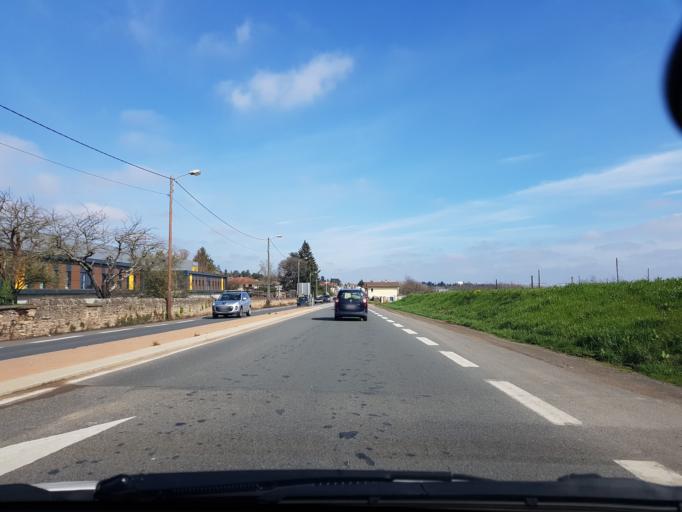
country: FR
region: Rhone-Alpes
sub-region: Departement du Rhone
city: Limas
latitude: 45.9608
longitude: 4.7156
